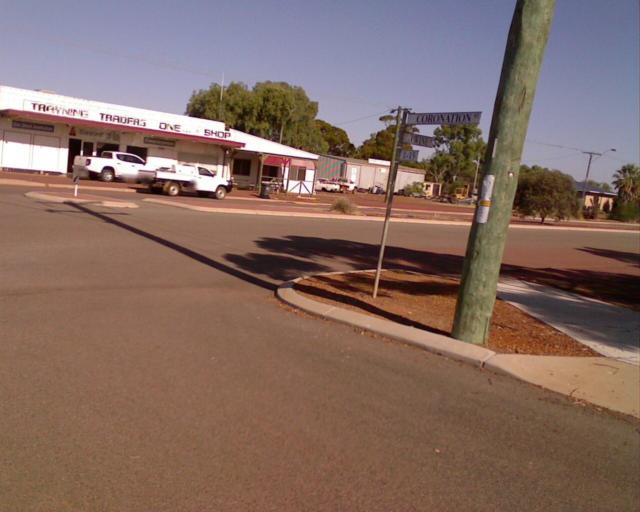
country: AU
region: Western Australia
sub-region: Merredin
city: Merredin
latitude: -31.1155
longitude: 117.7923
